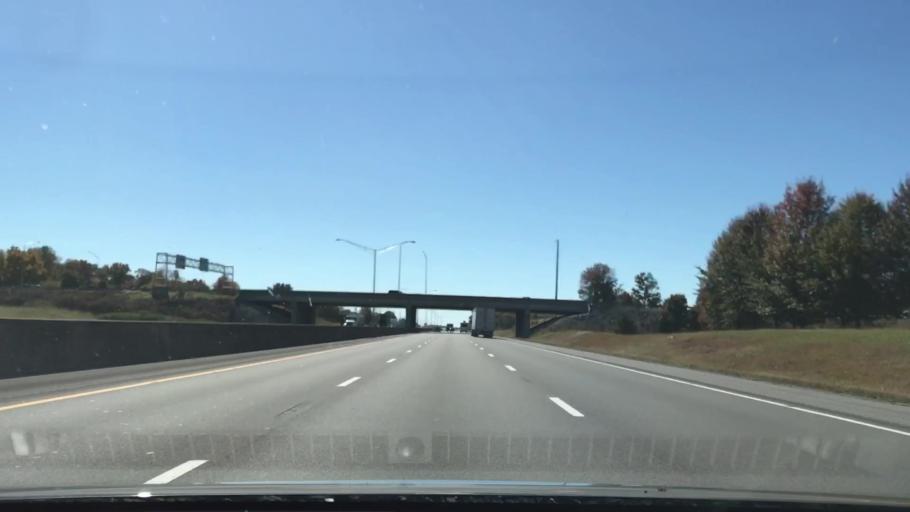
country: US
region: Kentucky
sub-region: Warren County
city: Bowling Green
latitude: 36.9794
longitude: -86.3894
